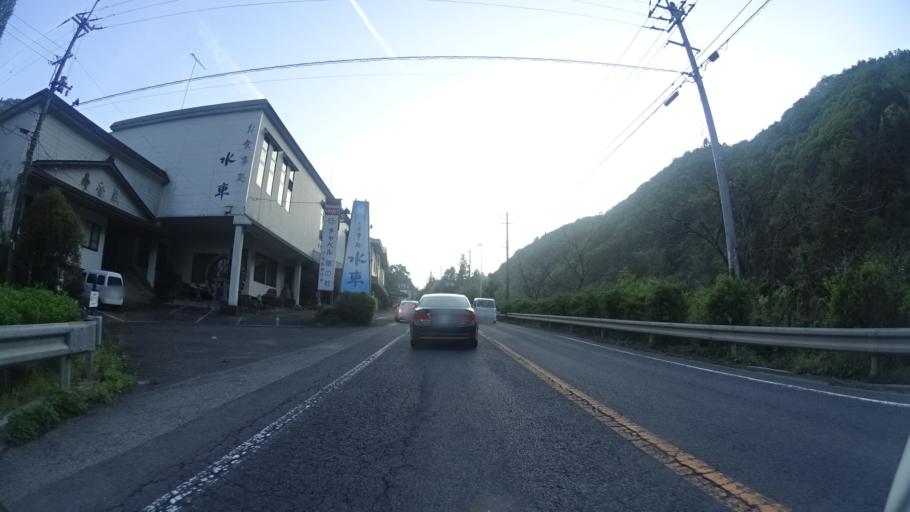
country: JP
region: Ehime
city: Kawanoecho
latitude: 33.9974
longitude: 133.6912
